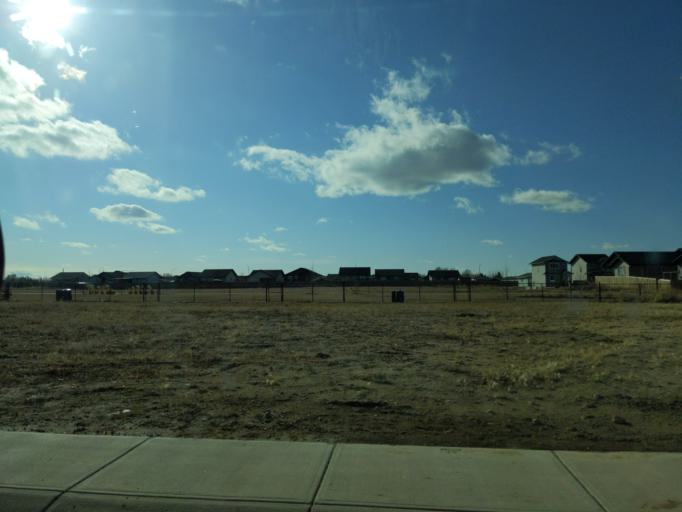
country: CA
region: Saskatchewan
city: Lloydminster
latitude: 53.2679
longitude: -109.9818
